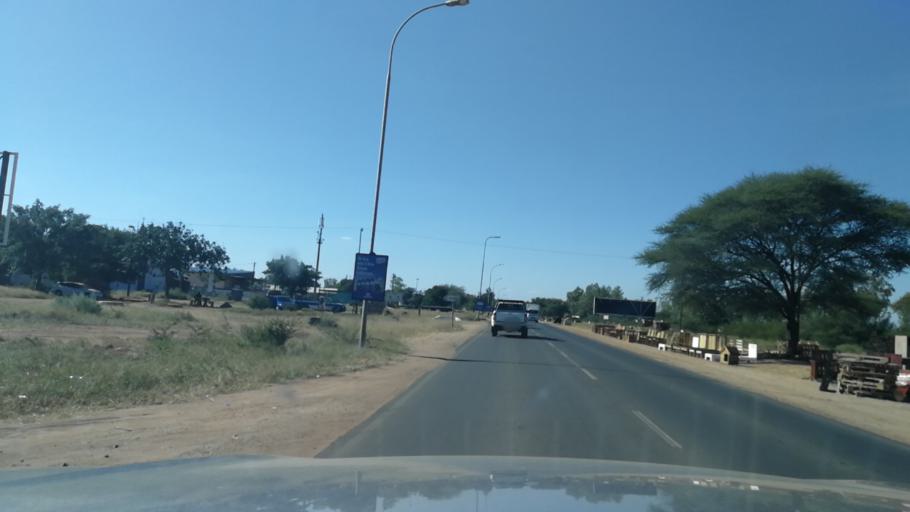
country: BW
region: South East
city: Gaborone
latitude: -24.6936
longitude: 25.8966
